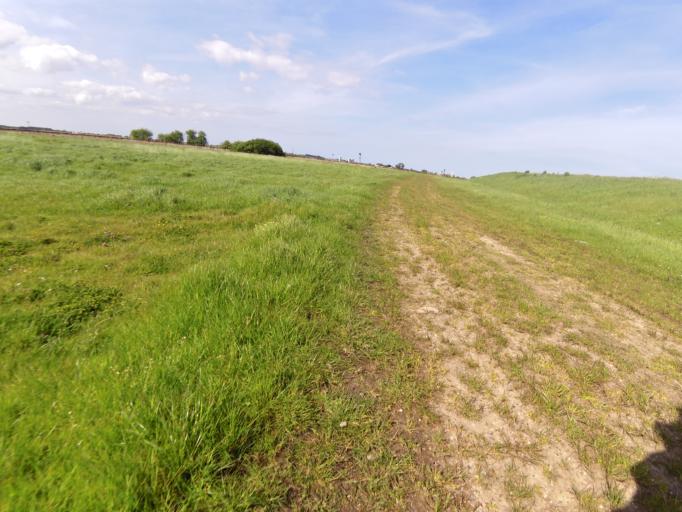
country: GB
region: England
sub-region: Norfolk
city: Great Yarmouth
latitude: 52.6167
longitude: 1.6925
